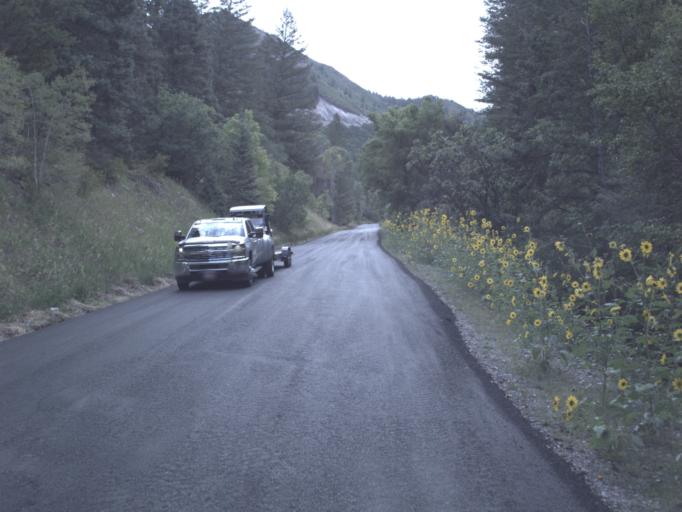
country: US
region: Utah
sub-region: Utah County
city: Cedar Hills
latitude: 40.4495
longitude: -111.6470
